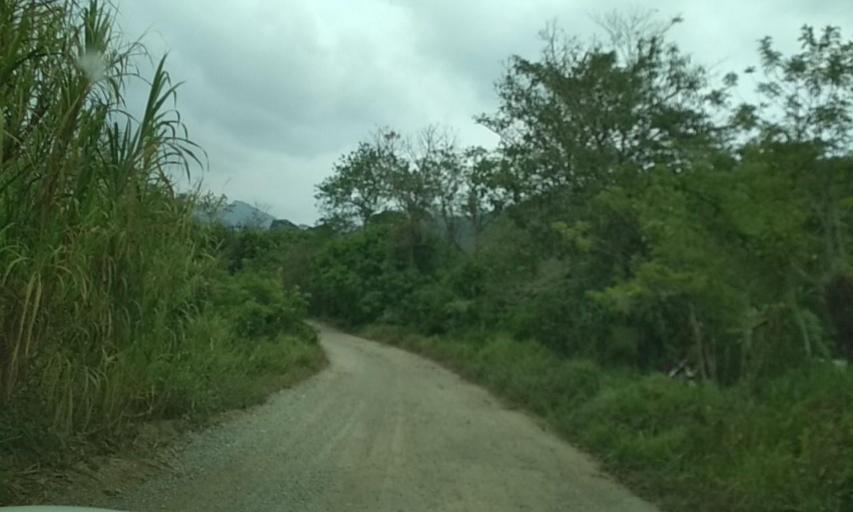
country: MX
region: Veracruz
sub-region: Uxpanapa
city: Poblado 10
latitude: 17.4955
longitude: -94.1318
